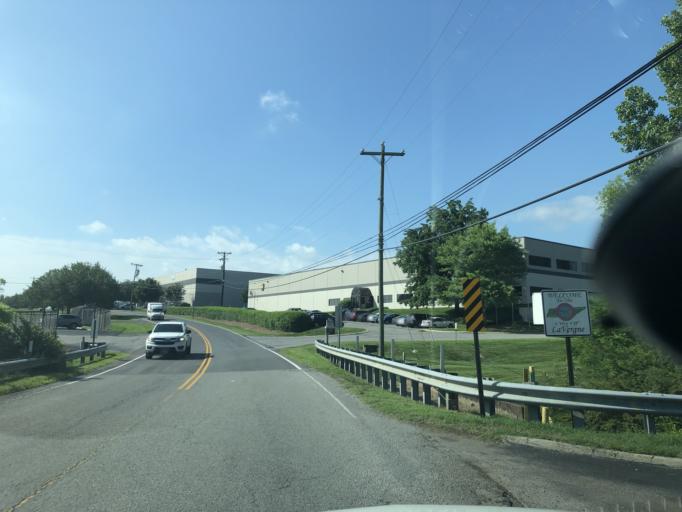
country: US
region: Tennessee
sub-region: Rutherford County
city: La Vergne
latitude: 36.0103
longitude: -86.6124
